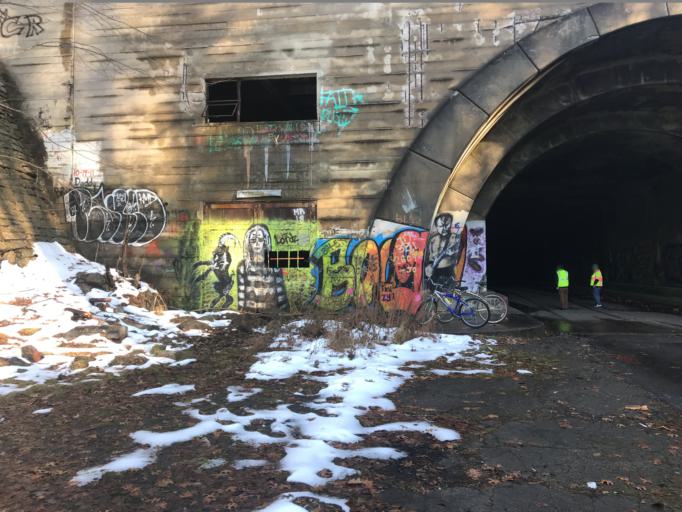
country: US
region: Pennsylvania
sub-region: Fulton County
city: McConnellsburg
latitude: 40.0497
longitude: -78.1412
